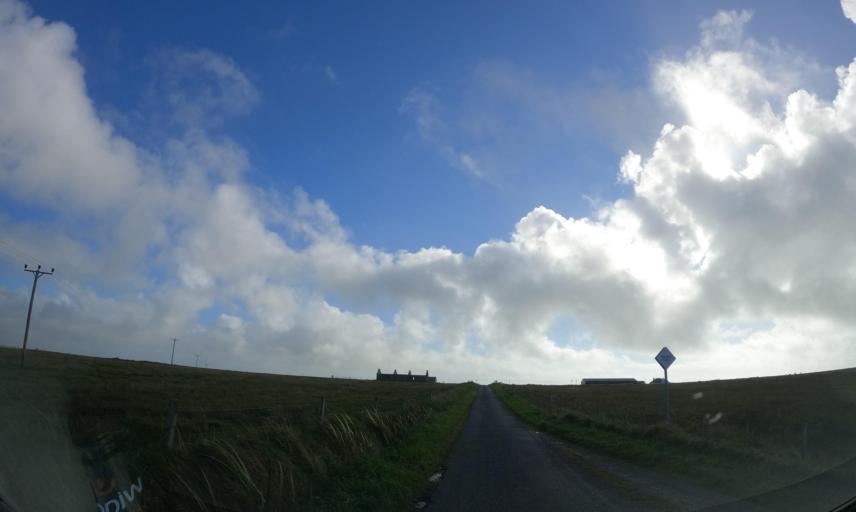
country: GB
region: Scotland
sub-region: Eilean Siar
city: Barra
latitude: 56.4836
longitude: -6.9221
